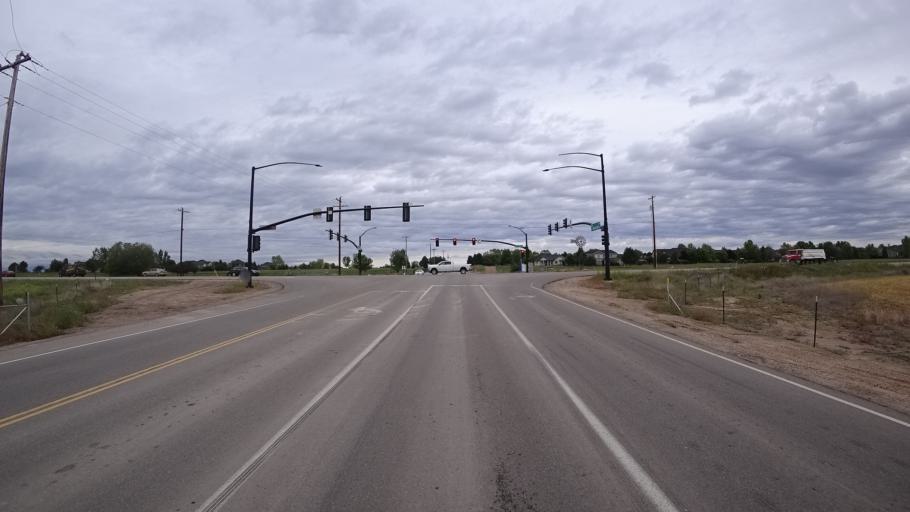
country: US
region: Idaho
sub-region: Ada County
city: Star
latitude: 43.7210
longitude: -116.4578
